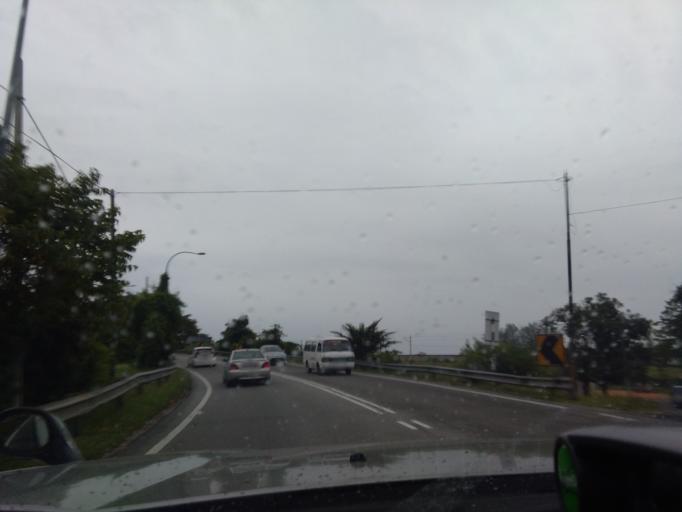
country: MY
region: Penang
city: Nibong Tebal
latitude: 5.1622
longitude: 100.4787
